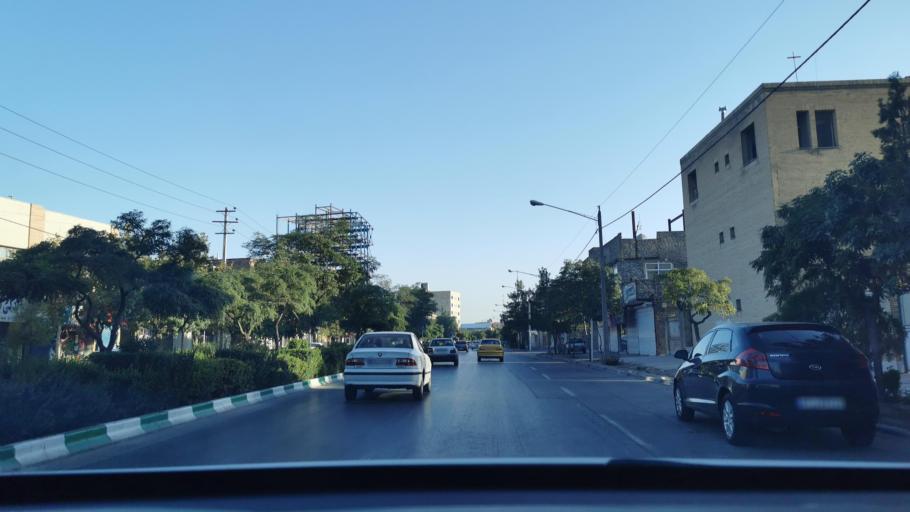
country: IR
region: Razavi Khorasan
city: Mashhad
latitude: 36.3533
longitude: 59.5134
